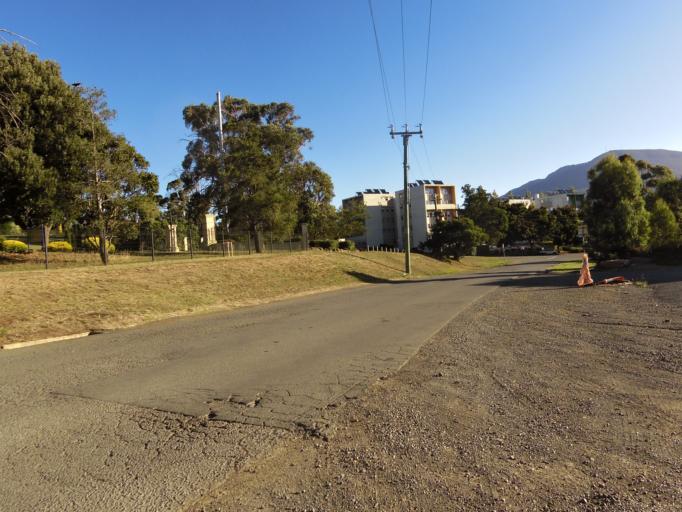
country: AU
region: Tasmania
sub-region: Hobart
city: New Town
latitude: -42.8500
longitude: 147.3164
